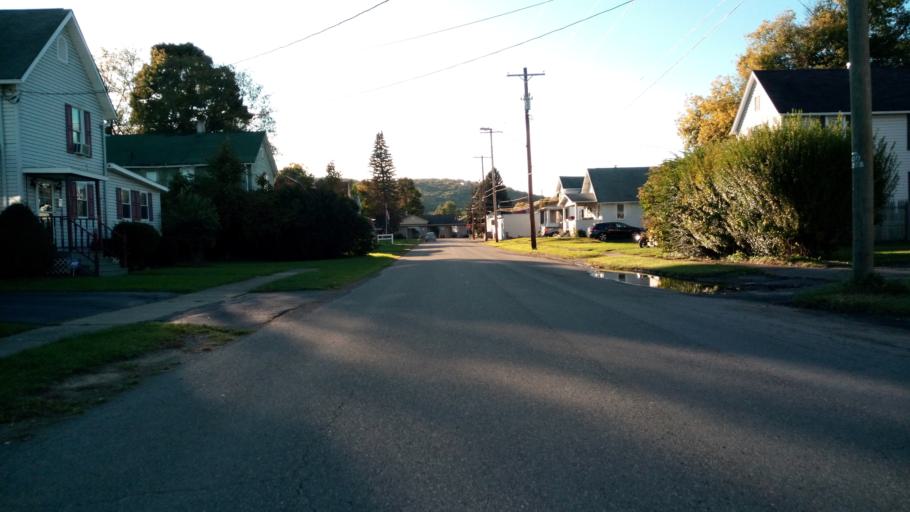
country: US
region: New York
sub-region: Chemung County
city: Southport
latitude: 42.0640
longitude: -76.8065
